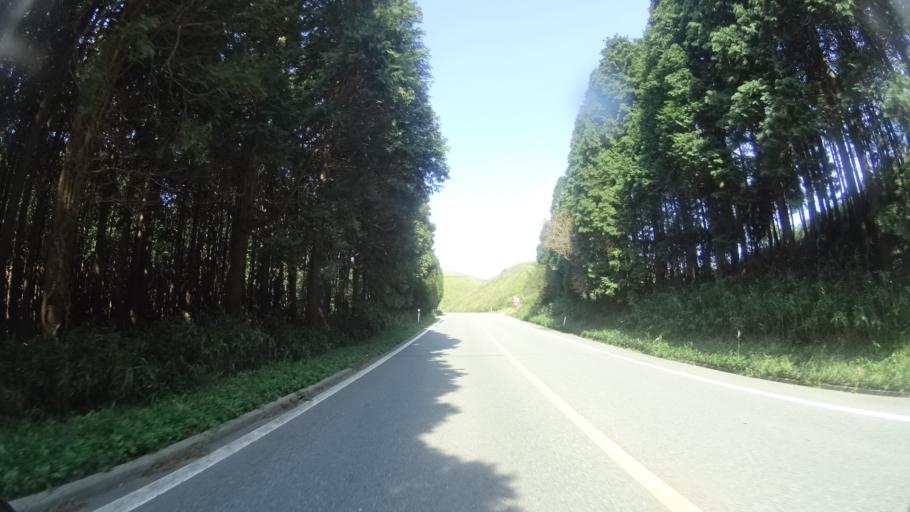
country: JP
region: Kumamoto
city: Ozu
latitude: 32.9187
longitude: 130.9674
